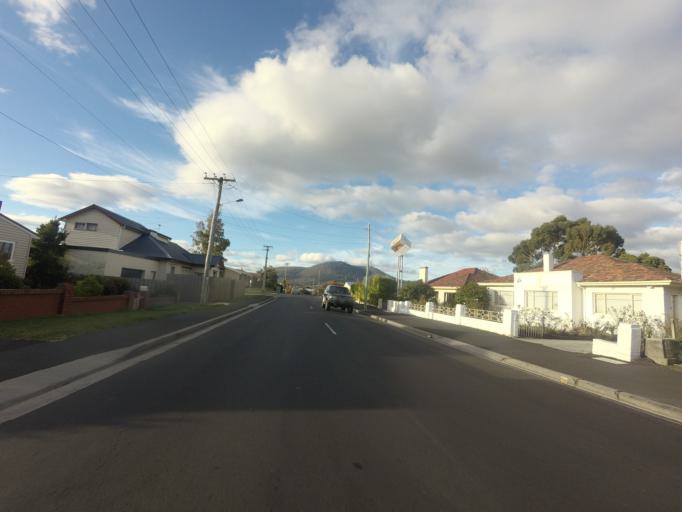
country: AU
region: Tasmania
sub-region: Glenorchy
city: Glenorchy
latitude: -42.8273
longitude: 147.2714
